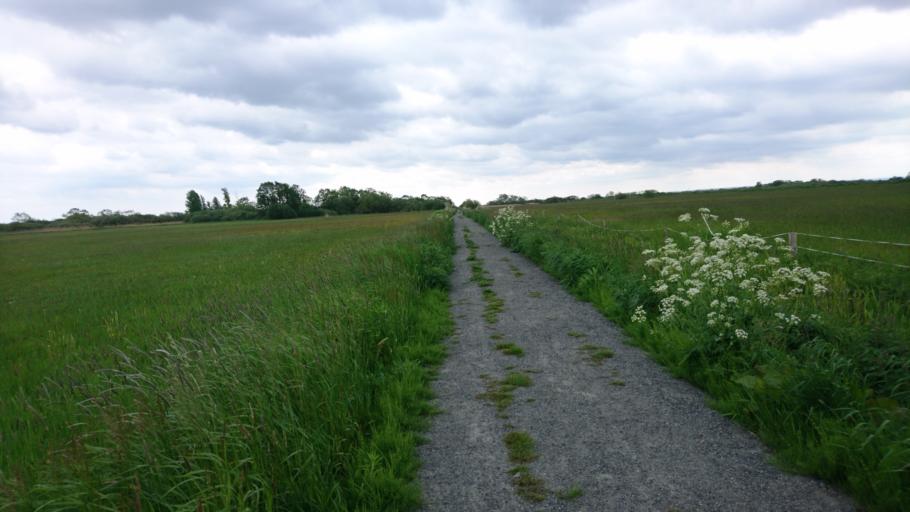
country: SE
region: Skane
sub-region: Kristianstads Kommun
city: Fjalkinge
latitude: 56.0062
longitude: 14.2416
